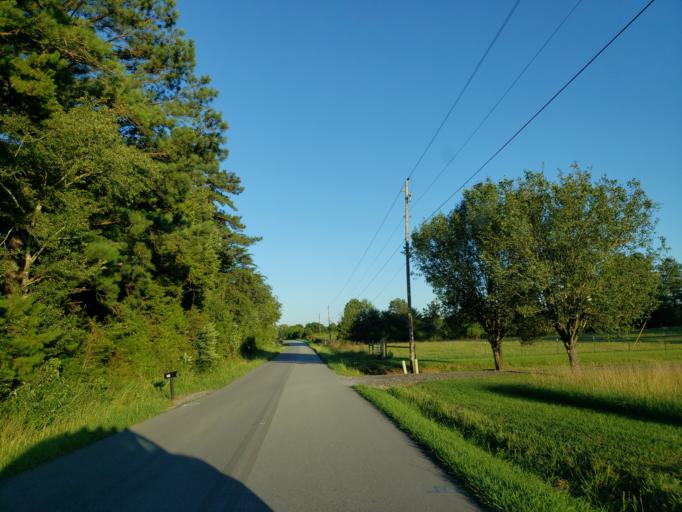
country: US
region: Georgia
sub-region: Bartow County
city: Euharlee
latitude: 34.0764
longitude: -84.9743
